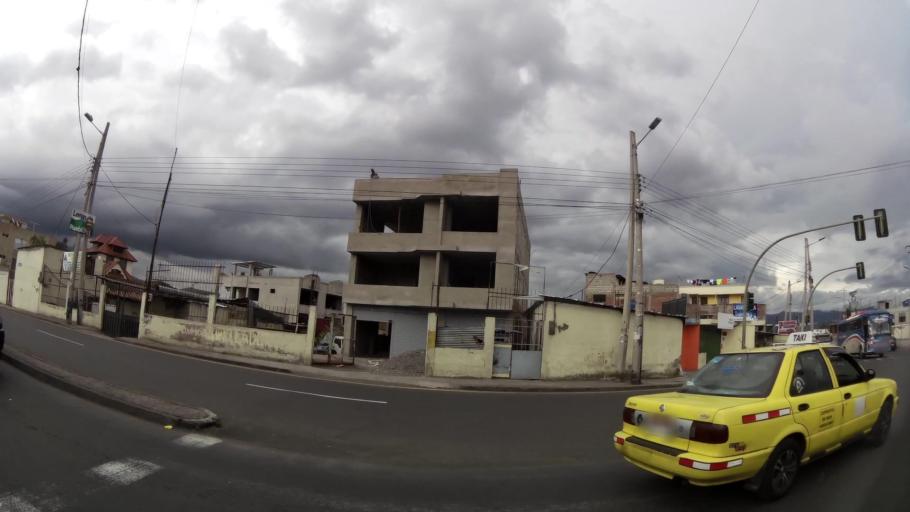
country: EC
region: Tungurahua
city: Ambato
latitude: -1.2768
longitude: -78.6256
